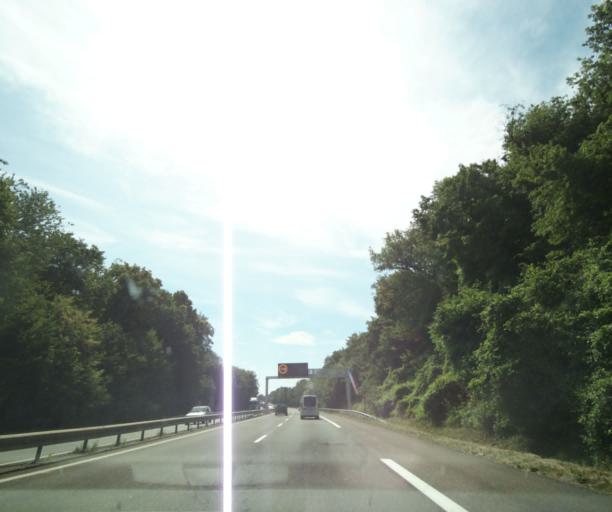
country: FR
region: Lorraine
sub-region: Departement de Meurthe-et-Moselle
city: Chavigny
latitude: 48.6504
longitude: 6.1322
